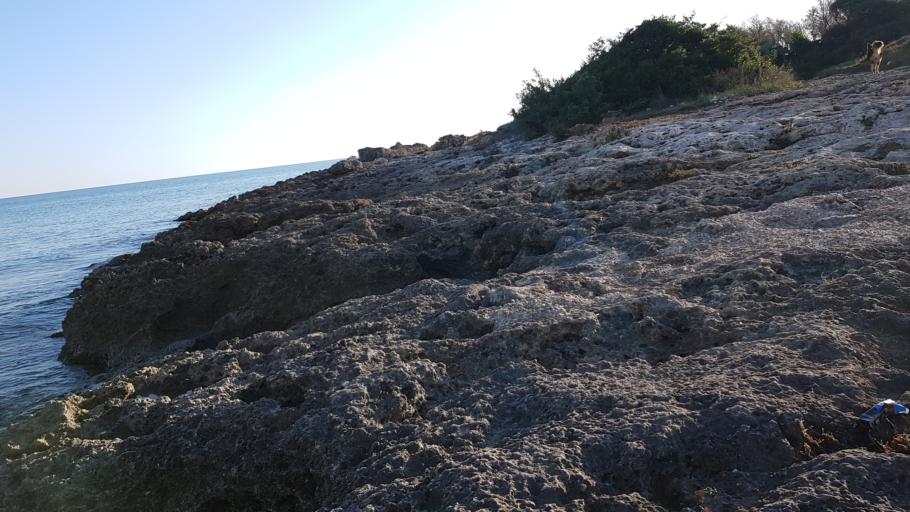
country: IT
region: Apulia
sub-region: Provincia di Taranto
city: Avetrana
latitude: 40.2930
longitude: 17.7666
